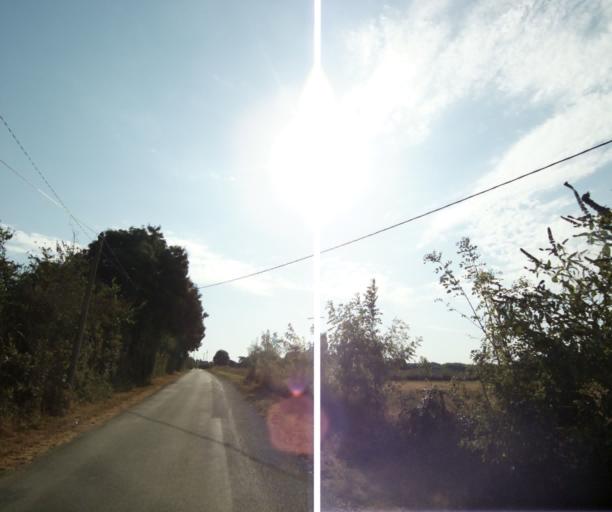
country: FR
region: Poitou-Charentes
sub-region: Departement de la Charente-Maritime
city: Tonnay-Charente
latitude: 45.9630
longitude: -0.8807
